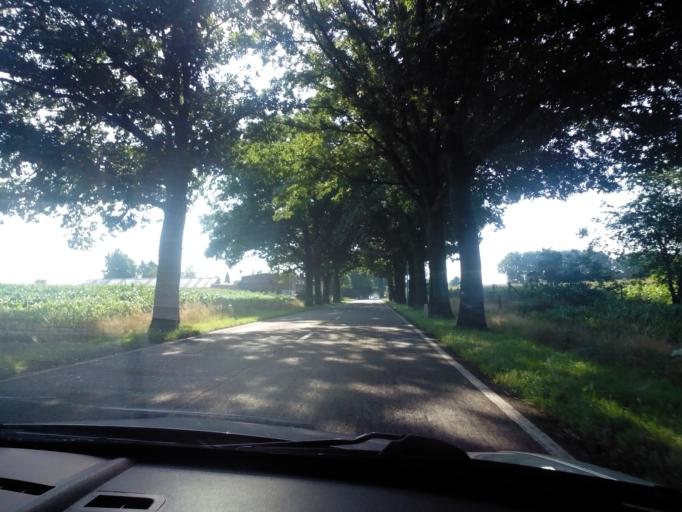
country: BE
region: Flanders
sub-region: Provincie Limburg
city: Bree
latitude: 51.0921
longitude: 5.6051
